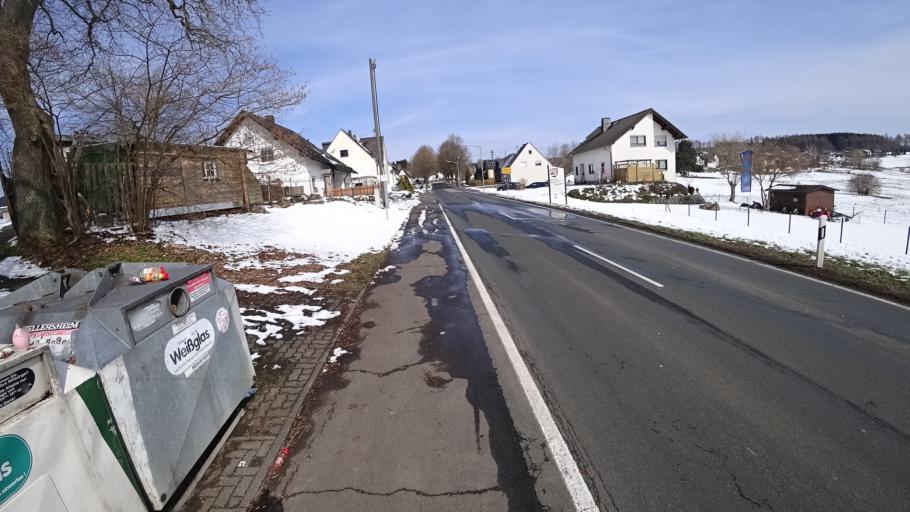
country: DE
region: Rheinland-Pfalz
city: Morlen
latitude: 50.6949
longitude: 7.8861
